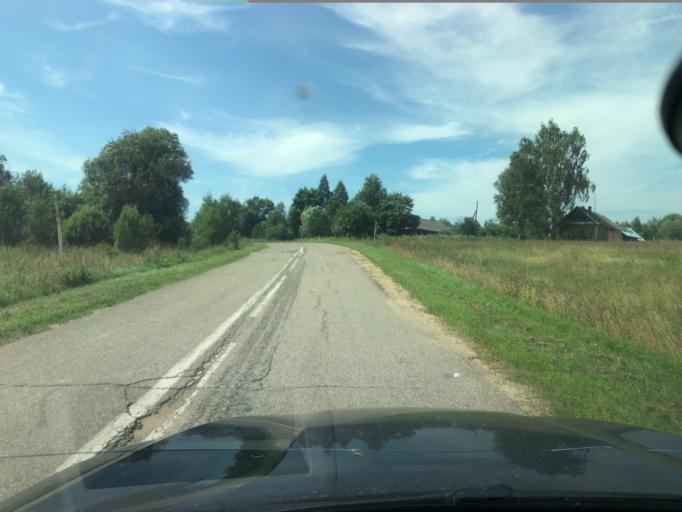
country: RU
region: Jaroslavl
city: Pereslavl'-Zalesskiy
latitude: 57.0385
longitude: 38.8969
